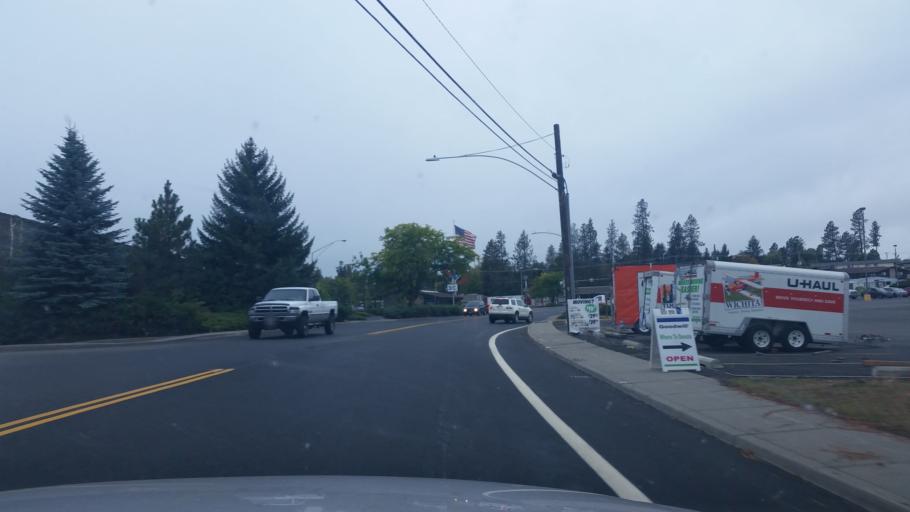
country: US
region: Washington
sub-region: Spokane County
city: Cheney
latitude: 47.4990
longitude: -117.5619
